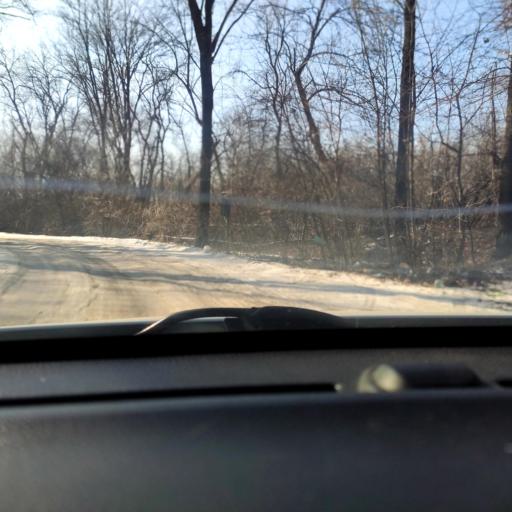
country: RU
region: Voronezj
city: Voronezh
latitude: 51.6657
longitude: 39.1315
